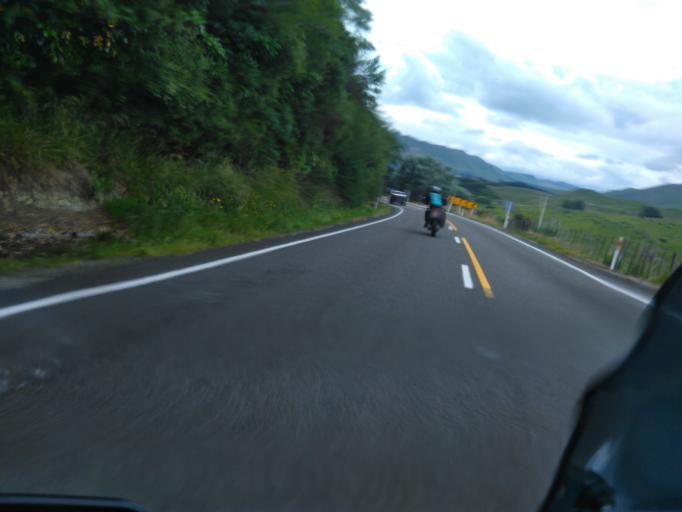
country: NZ
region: Bay of Plenty
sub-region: Opotiki District
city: Opotiki
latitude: -38.3977
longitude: 177.5605
